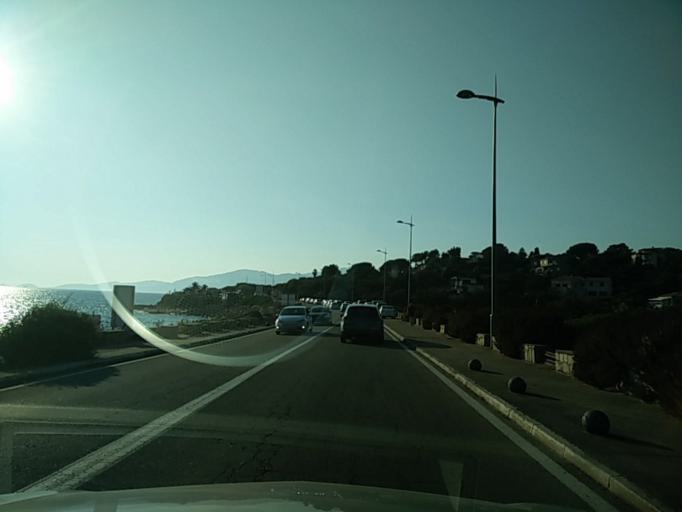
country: FR
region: Corsica
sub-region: Departement de la Corse-du-Sud
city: Pietrosella
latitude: 41.8676
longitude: 8.7903
